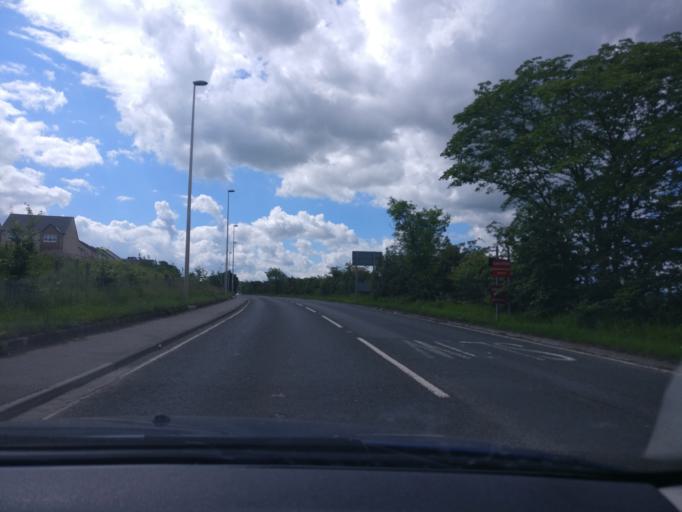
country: GB
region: Scotland
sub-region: Midlothian
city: Gorebridge
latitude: 55.8557
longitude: -3.0654
